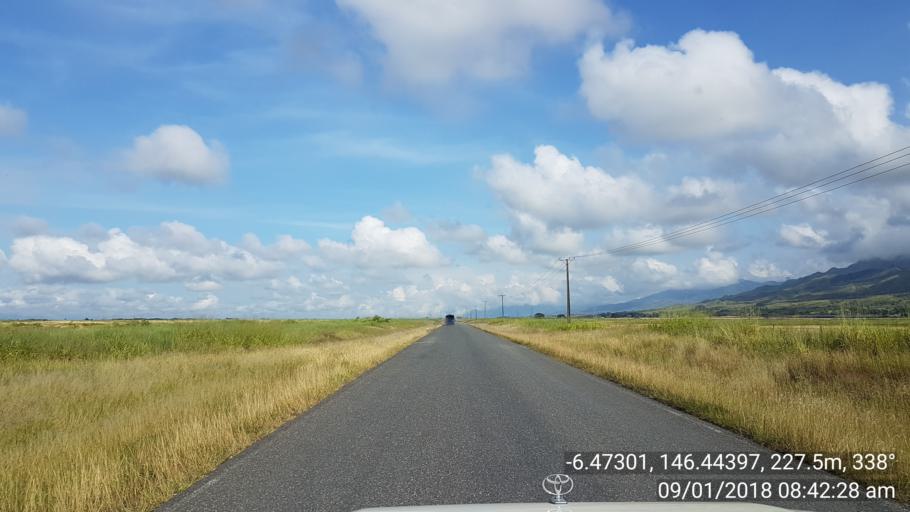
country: PG
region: Morobe
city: Lae
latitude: -6.4731
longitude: 146.4441
